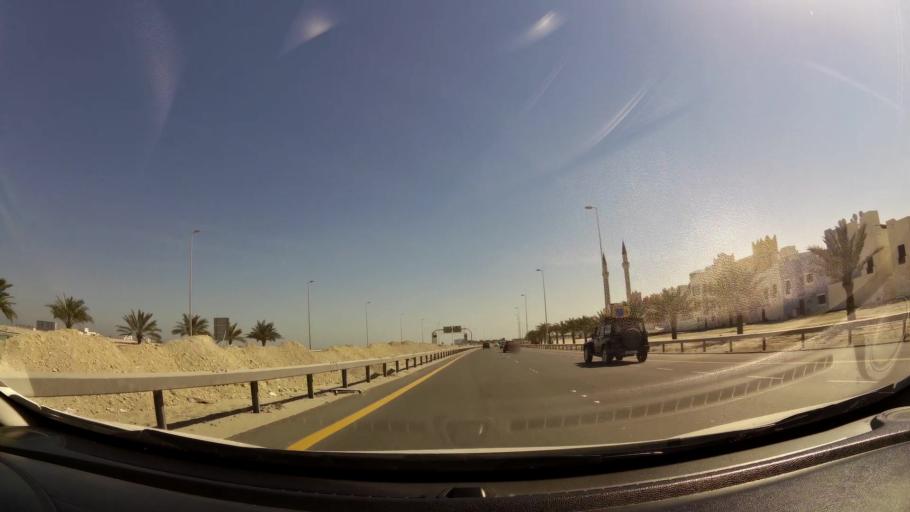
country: BH
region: Muharraq
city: Al Hadd
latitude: 26.2728
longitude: 50.6608
